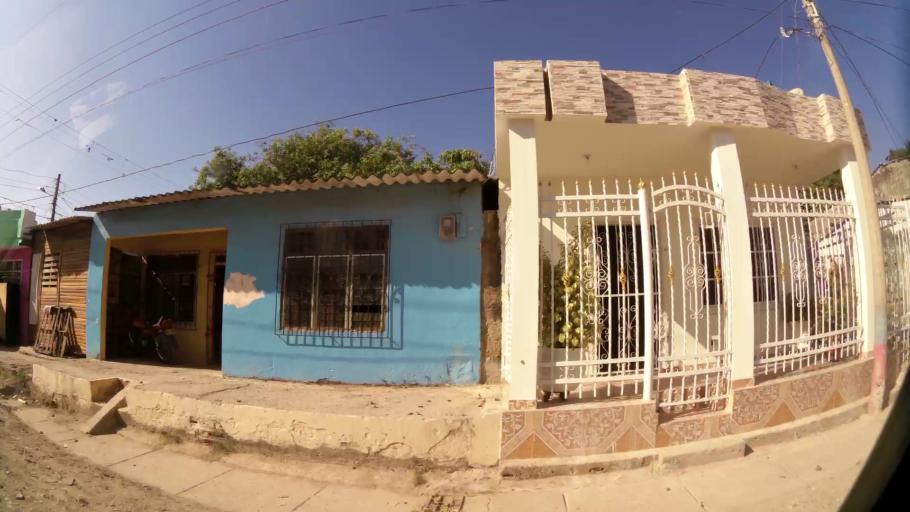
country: CO
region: Bolivar
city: Cartagena
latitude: 10.4153
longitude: -75.5179
